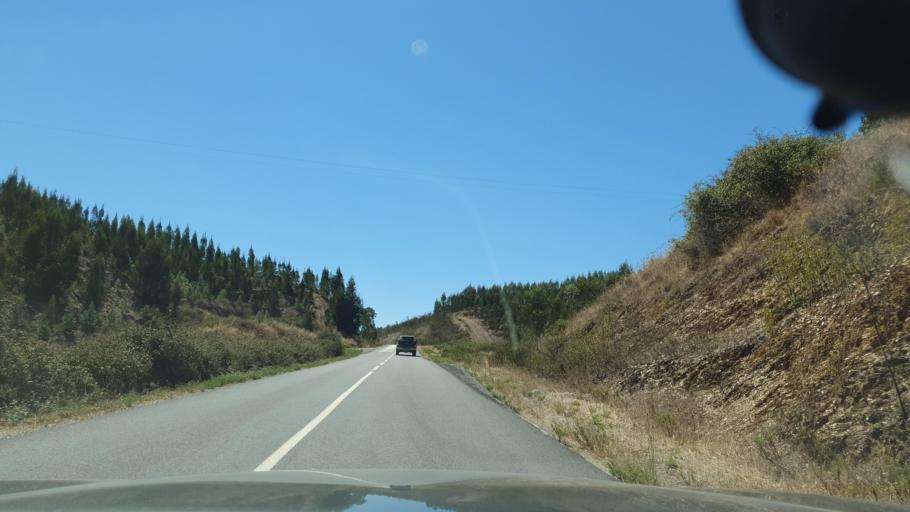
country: PT
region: Faro
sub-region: Monchique
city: Monchique
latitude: 37.4325
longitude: -8.5286
